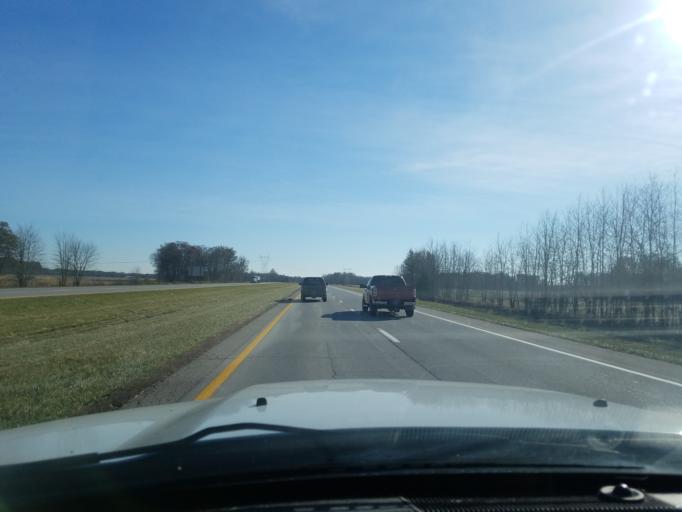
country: US
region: Ohio
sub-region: Brown County
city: Mount Orab
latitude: 39.0343
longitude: -83.8989
